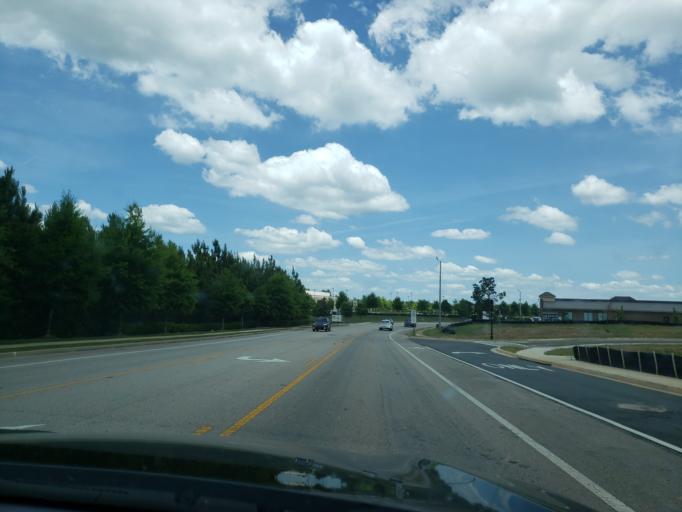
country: US
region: Alabama
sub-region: Lee County
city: Auburn
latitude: 32.6029
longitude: -85.4428
